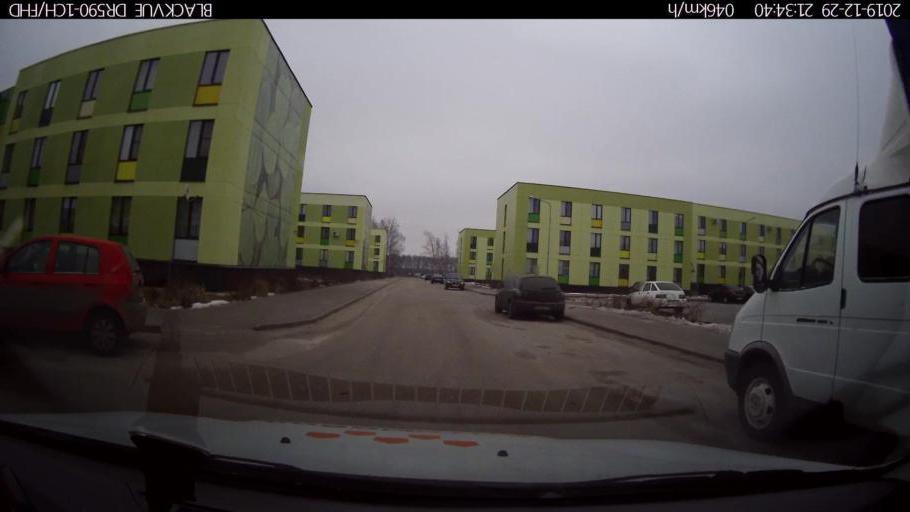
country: RU
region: Nizjnij Novgorod
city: Afonino
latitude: 56.2149
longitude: 44.0210
